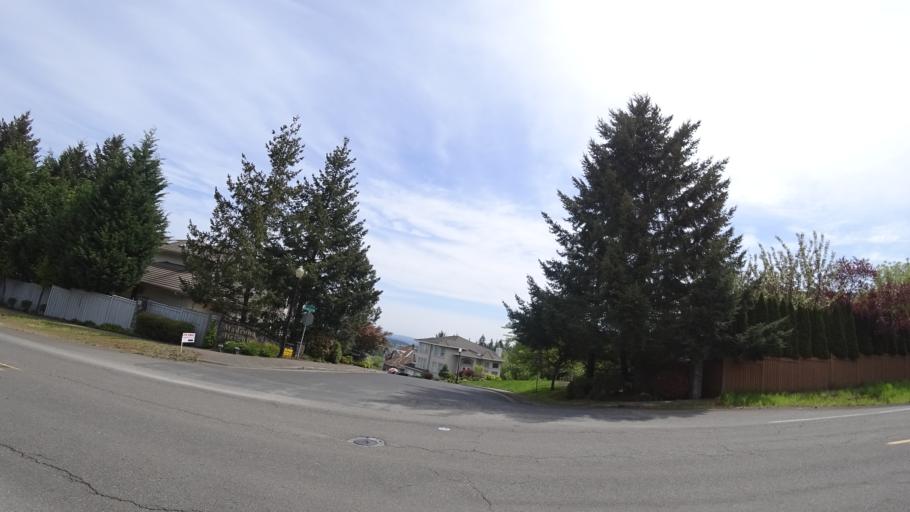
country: US
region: Oregon
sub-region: Washington County
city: Aloha
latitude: 45.4550
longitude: -122.8569
